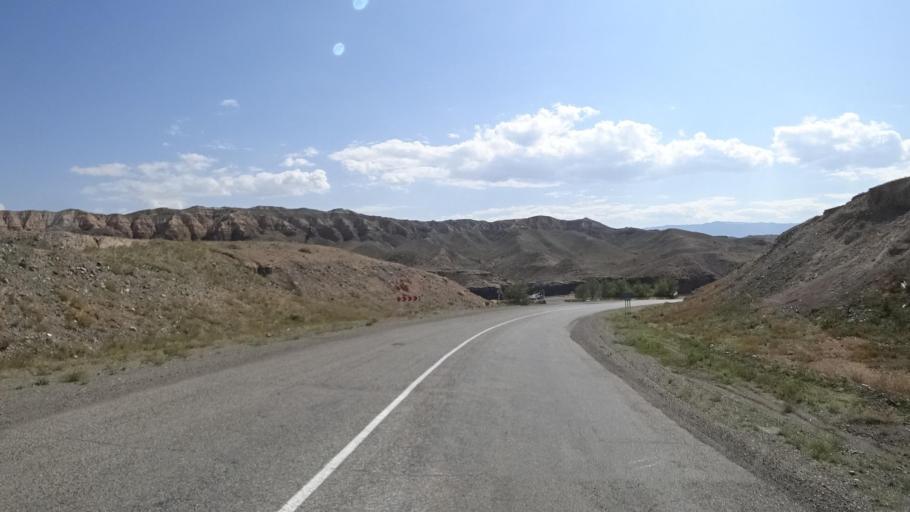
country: KZ
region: Almaty Oblysy
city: Kegen
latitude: 43.2708
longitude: 78.9720
